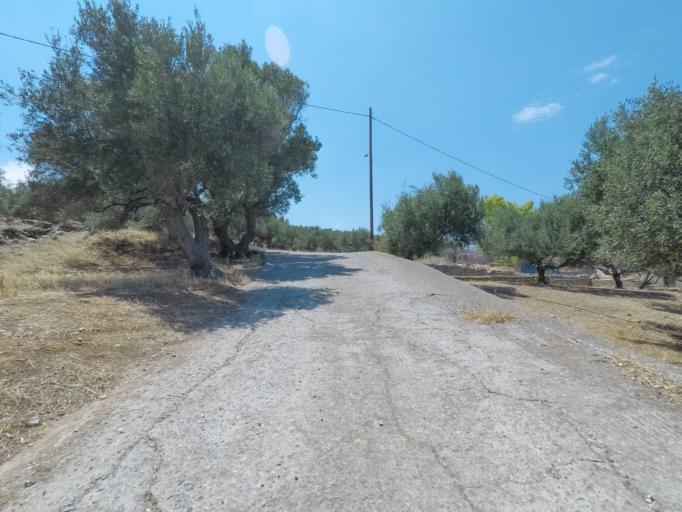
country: GR
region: Crete
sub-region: Nomos Lasithiou
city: Elounda
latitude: 35.3149
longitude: 25.7342
